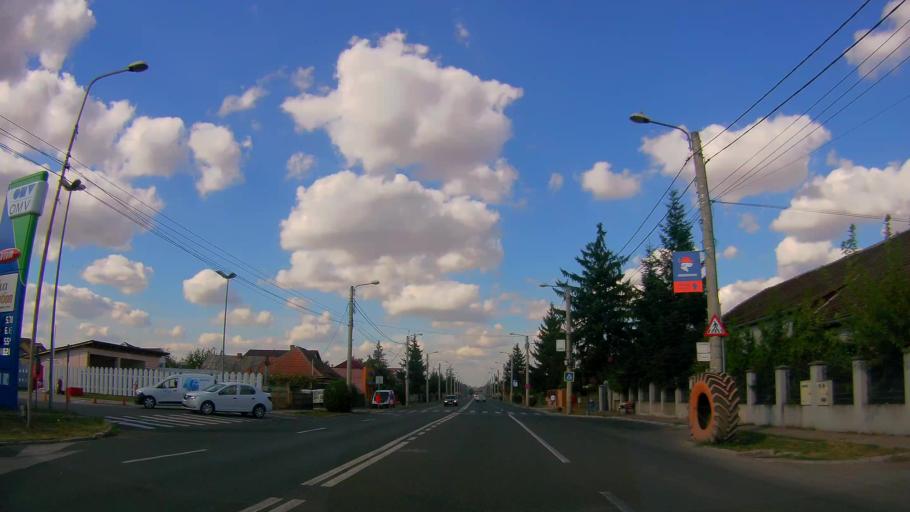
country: RO
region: Satu Mare
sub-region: Municipiul Satu Mare
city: Satu Mare
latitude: 47.7629
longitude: 22.8835
